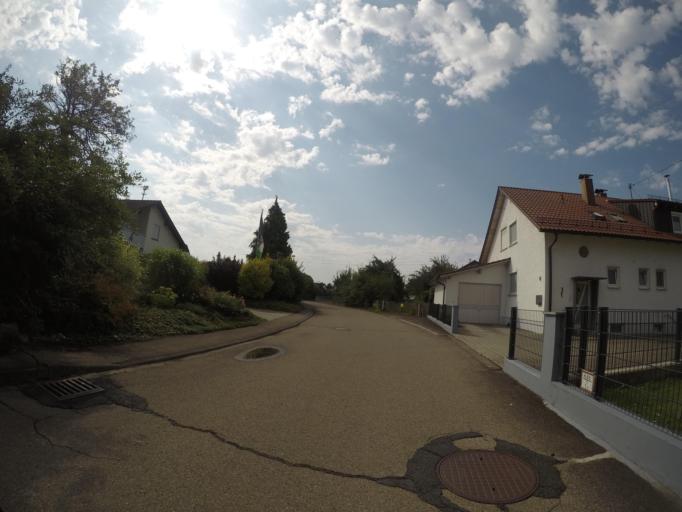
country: DE
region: Baden-Wuerttemberg
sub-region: Tuebingen Region
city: Dietenheim
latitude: 48.1769
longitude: 10.0784
